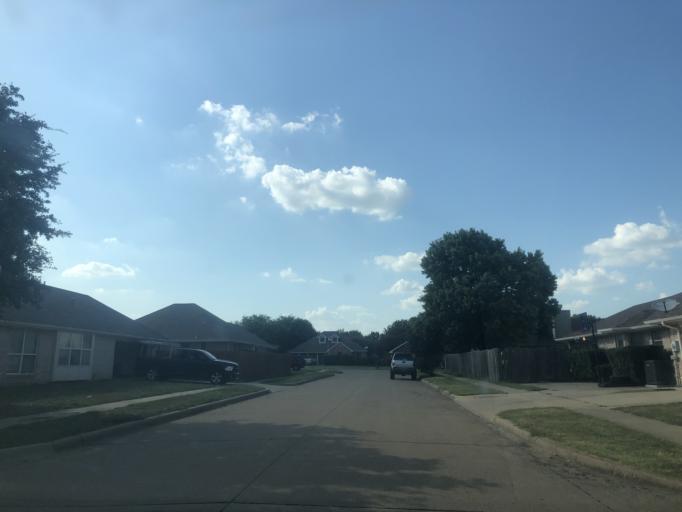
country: US
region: Texas
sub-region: Tarrant County
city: Saginaw
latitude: 32.8535
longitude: -97.3865
